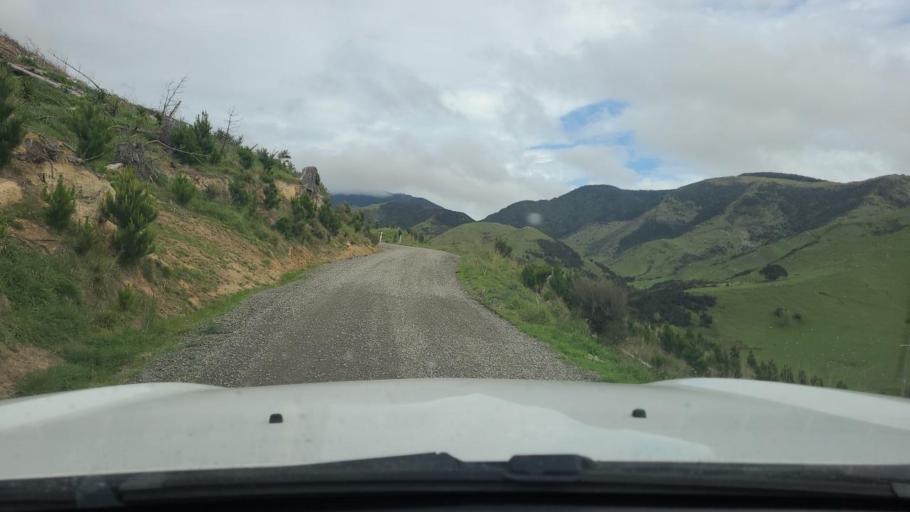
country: NZ
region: Wellington
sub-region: South Wairarapa District
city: Waipawa
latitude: -41.3563
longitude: 175.3962
